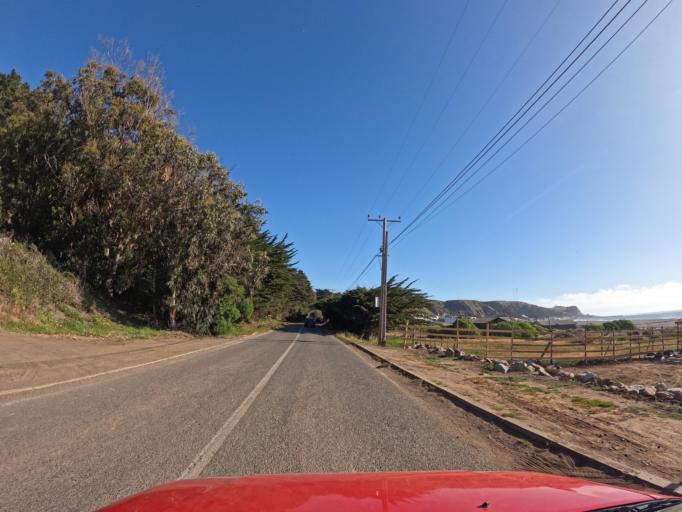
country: CL
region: Maule
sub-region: Provincia de Talca
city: Constitucion
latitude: -34.8781
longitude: -72.1553
